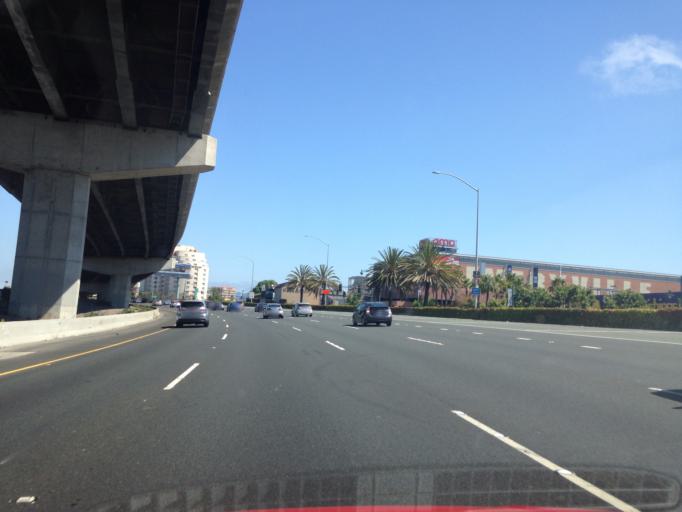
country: US
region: California
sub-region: Alameda County
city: Emeryville
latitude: 37.8308
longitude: -122.2932
